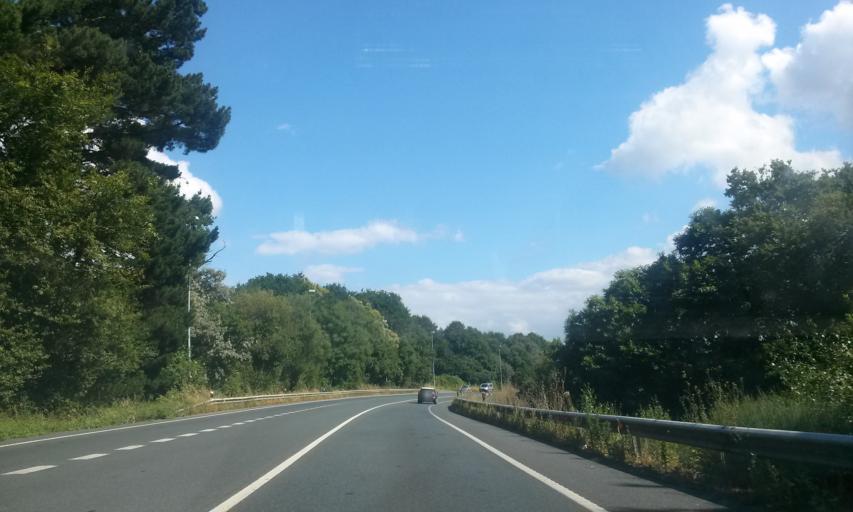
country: ES
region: Galicia
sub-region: Provincia de Lugo
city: Lugo
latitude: 43.0147
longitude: -7.5818
